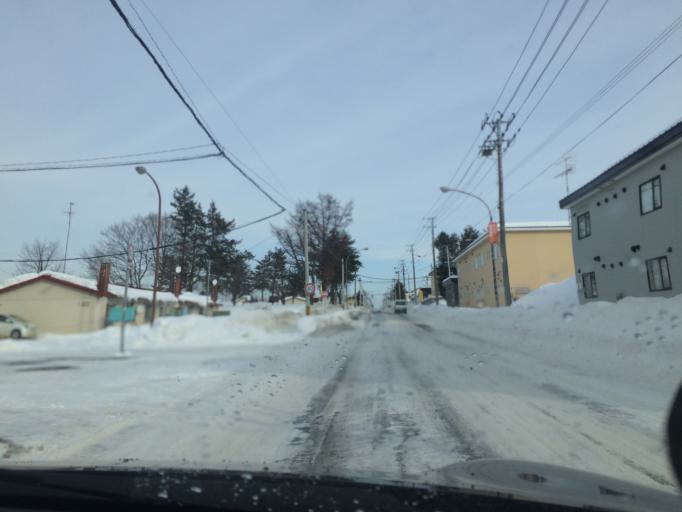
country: JP
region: Hokkaido
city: Obihiro
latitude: 42.9102
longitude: 143.0402
